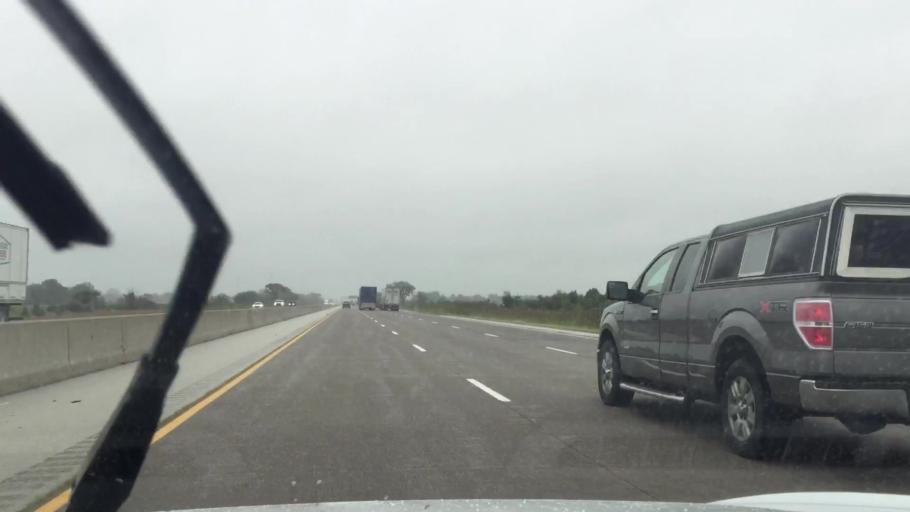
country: US
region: Michigan
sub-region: Wayne County
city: Grosse Pointe
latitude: 42.2367
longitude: -82.7342
